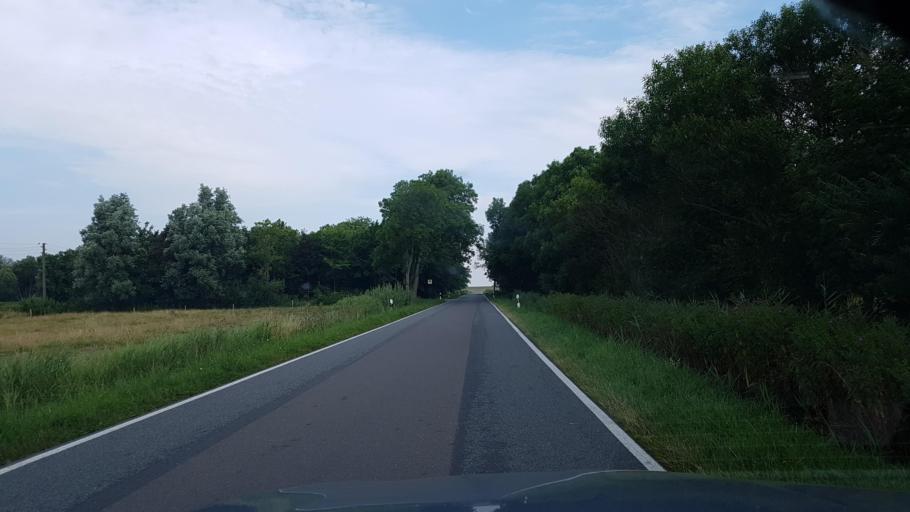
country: DE
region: Schleswig-Holstein
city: Tumlauer Koog
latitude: 54.3589
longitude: 8.7028
